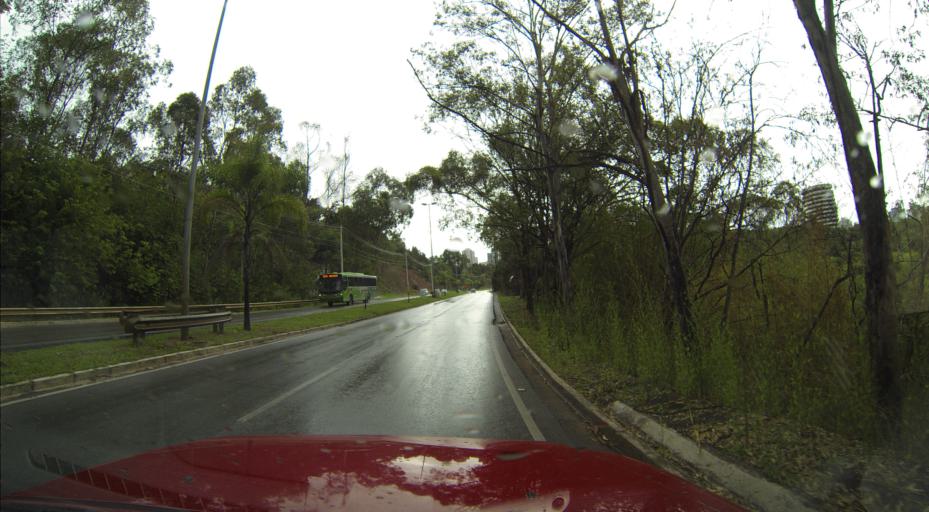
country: BR
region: Minas Gerais
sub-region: Belo Horizonte
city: Belo Horizonte
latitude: -19.9875
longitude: -43.9342
